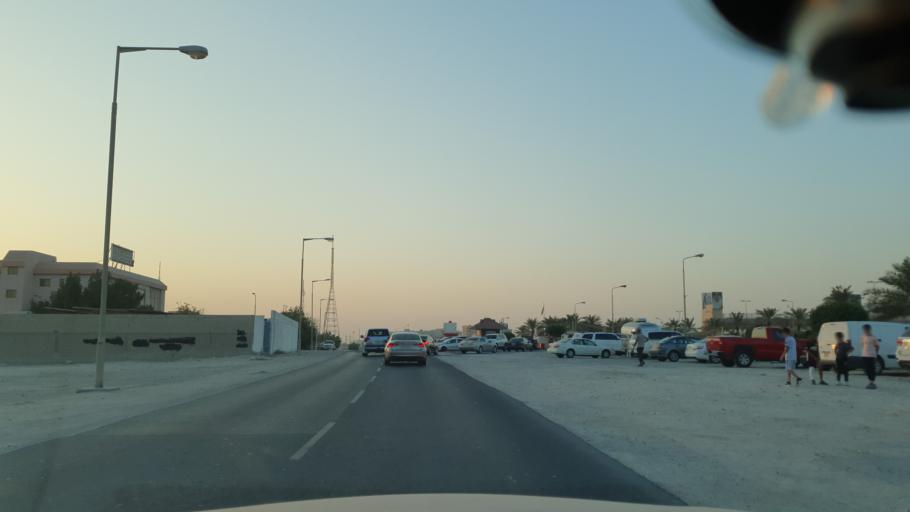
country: BH
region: Northern
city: Madinat `Isa
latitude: 26.1574
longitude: 50.5657
